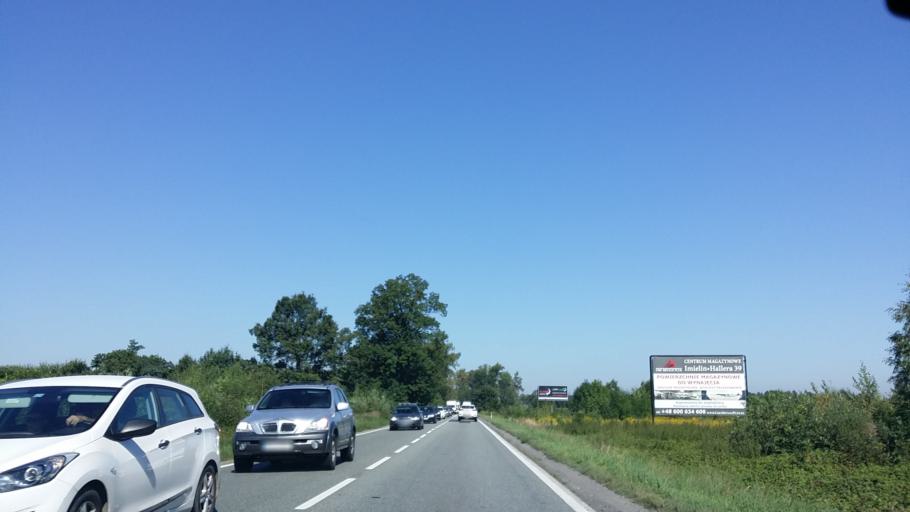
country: PL
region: Lesser Poland Voivodeship
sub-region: Powiat oswiecimski
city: Babice
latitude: 50.0590
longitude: 19.1964
